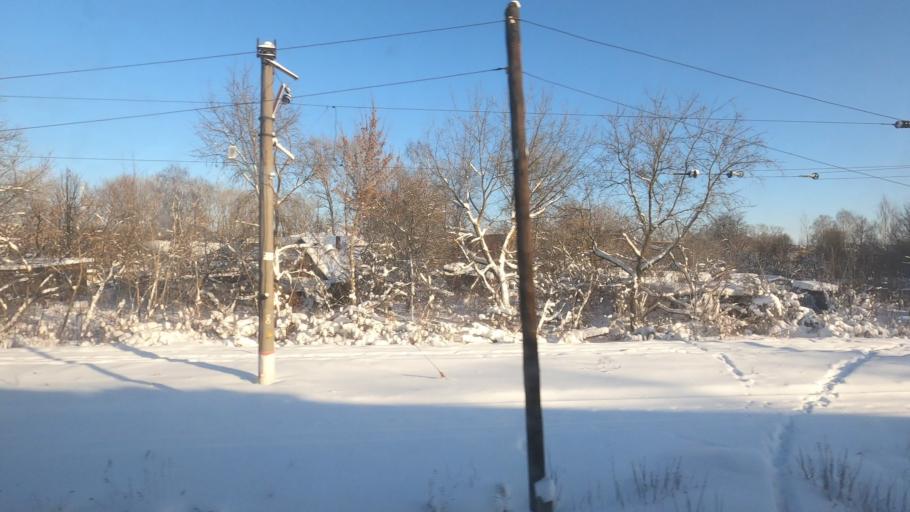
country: RU
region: Moskovskaya
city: Dmitrov
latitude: 56.3802
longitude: 37.5191
